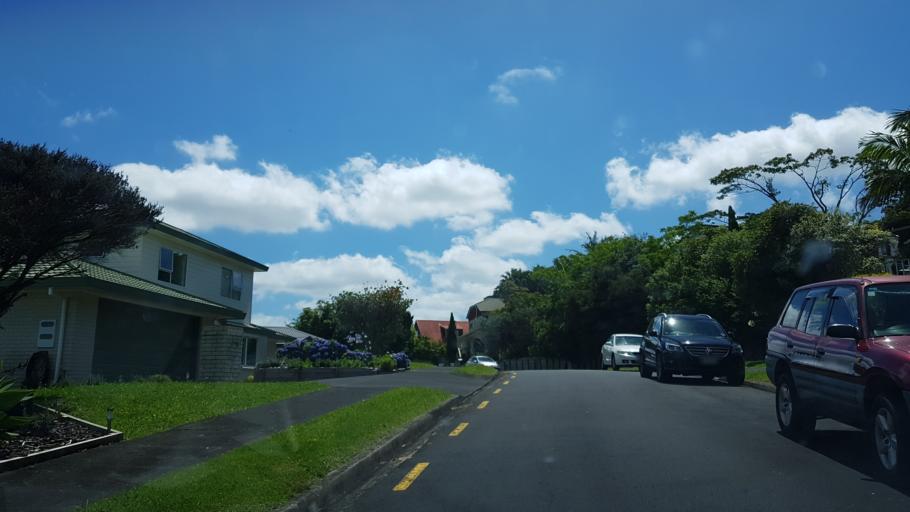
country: NZ
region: Auckland
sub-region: Auckland
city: North Shore
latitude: -36.7868
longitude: 174.7087
